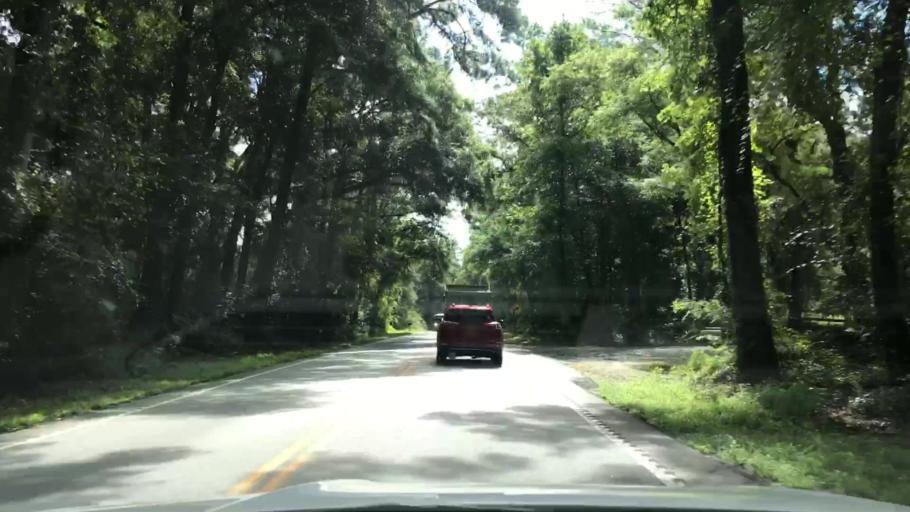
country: US
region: South Carolina
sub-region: Berkeley County
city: Ladson
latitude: 32.8886
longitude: -80.1206
